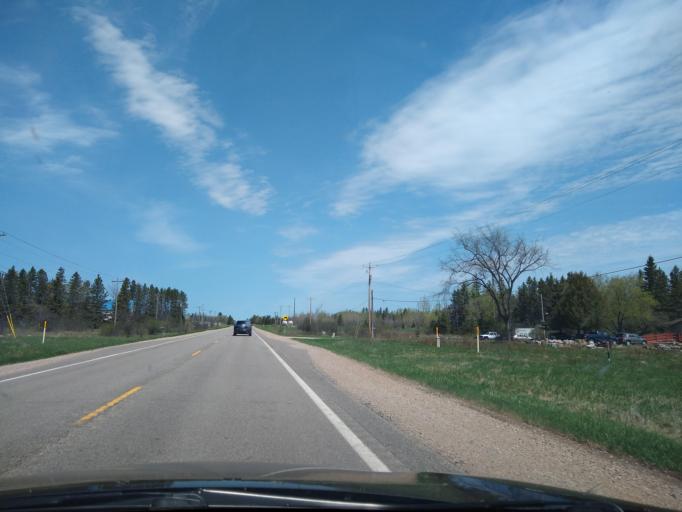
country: US
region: Michigan
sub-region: Delta County
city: Gladstone
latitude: 45.9401
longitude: -86.9720
